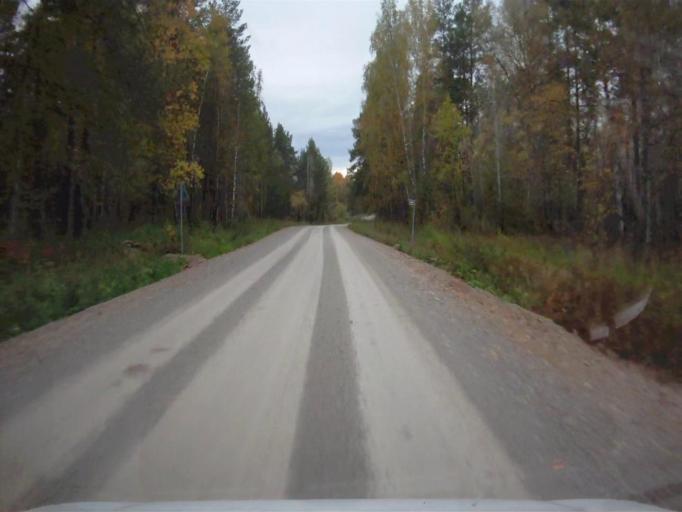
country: RU
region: Chelyabinsk
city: Nyazepetrovsk
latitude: 56.0718
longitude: 59.4297
